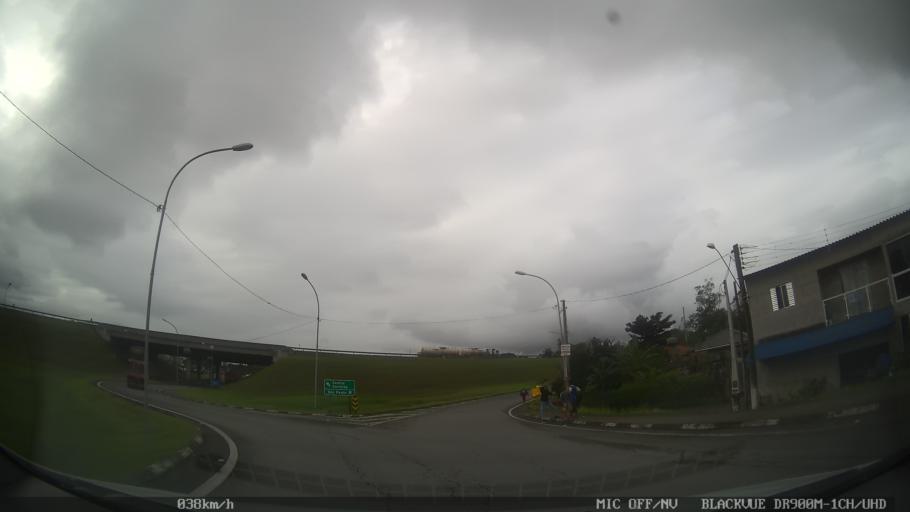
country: BR
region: Sao Paulo
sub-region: Cajati
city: Cajati
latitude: -24.7320
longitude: -48.0987
